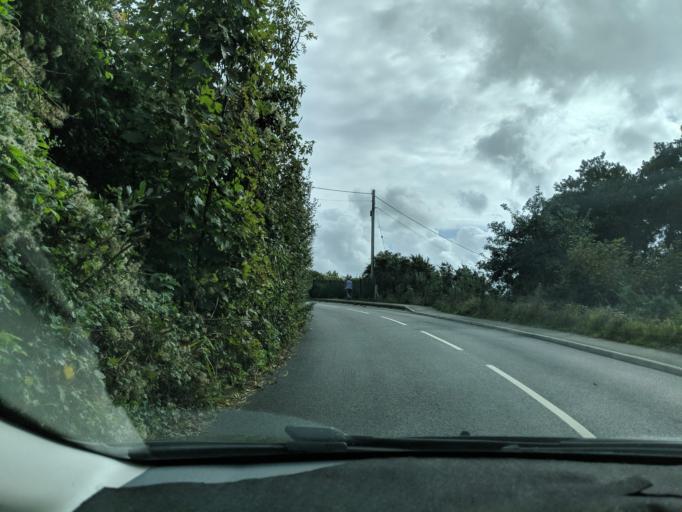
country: GB
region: England
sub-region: Cornwall
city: Par
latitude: 50.3573
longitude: -4.7048
